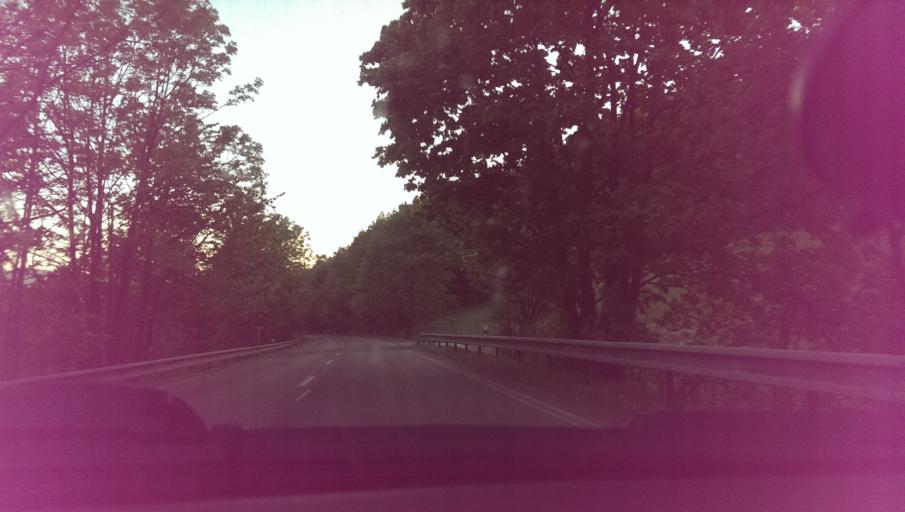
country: CZ
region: Zlin
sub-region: Okres Vsetin
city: Dolni Becva
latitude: 49.4923
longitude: 18.1723
